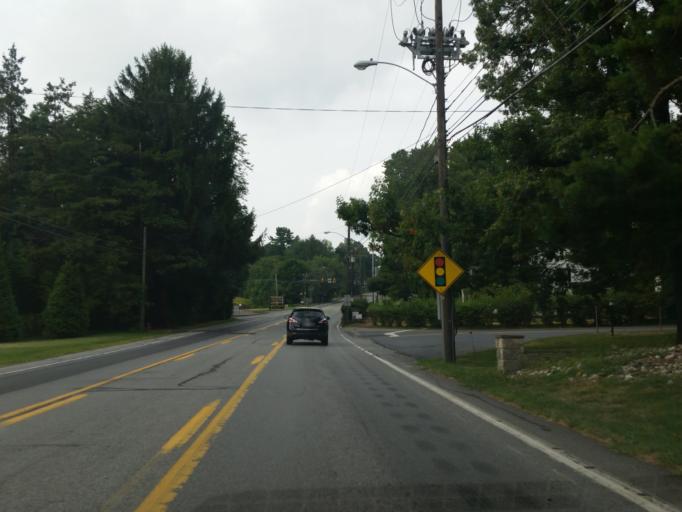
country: US
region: Pennsylvania
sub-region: Lancaster County
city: East Petersburg
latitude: 40.0903
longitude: -76.3044
